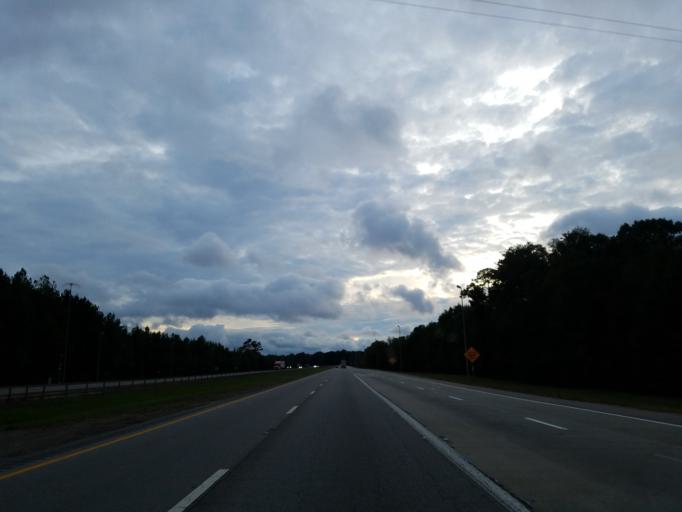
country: US
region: Alabama
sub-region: Sumter County
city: York
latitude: 32.4355
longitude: -88.4407
